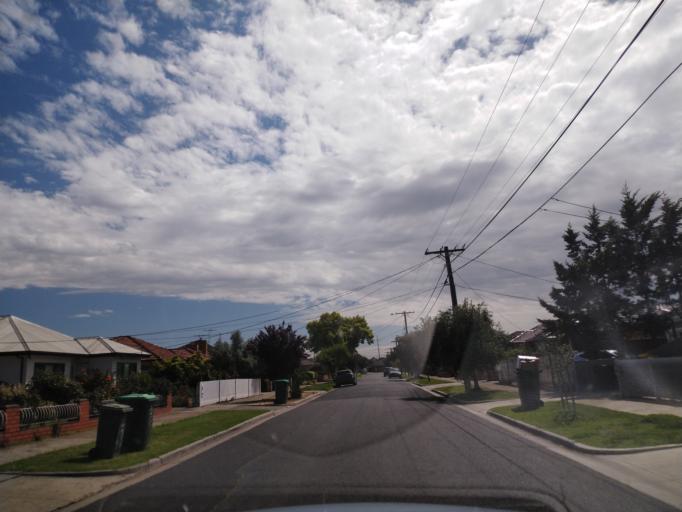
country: AU
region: Victoria
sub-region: Hobsons Bay
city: Altona North
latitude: -37.8307
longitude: 144.8554
